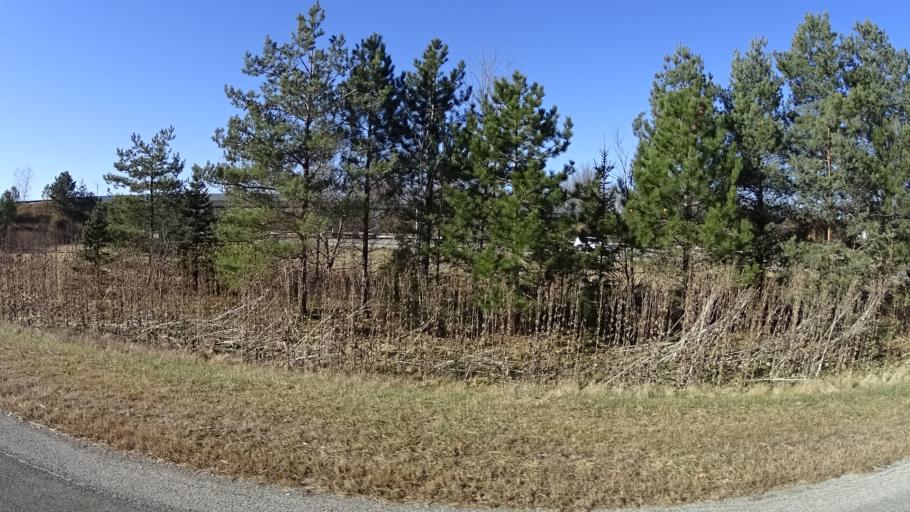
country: US
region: Ohio
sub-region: Lorain County
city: Oberlin
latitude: 41.2943
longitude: -82.1657
